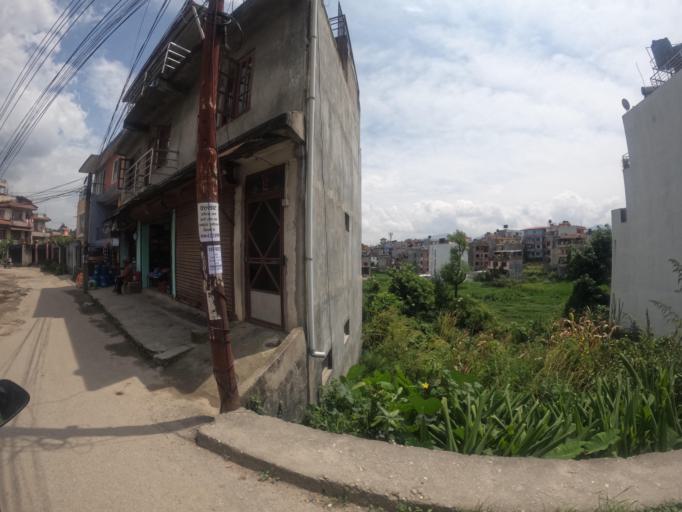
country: NP
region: Central Region
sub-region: Bagmati Zone
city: Kathmandu
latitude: 27.6796
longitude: 85.3666
